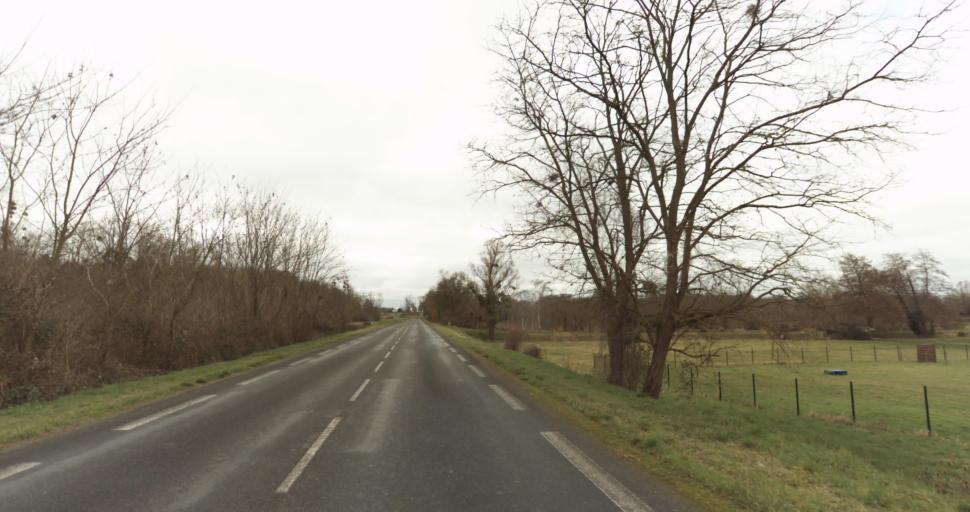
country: FR
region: Pays de la Loire
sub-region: Departement de Maine-et-Loire
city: Distre
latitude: 47.2186
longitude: -0.1135
